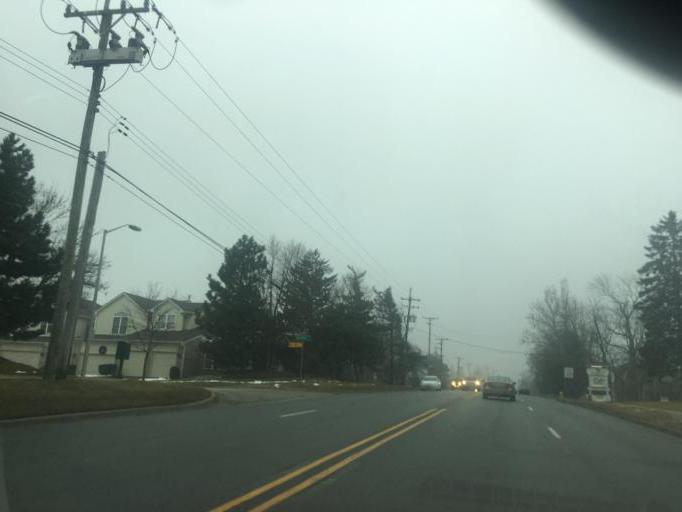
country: US
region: Illinois
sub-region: DuPage County
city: Downers Grove
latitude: 41.7885
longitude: -88.0377
